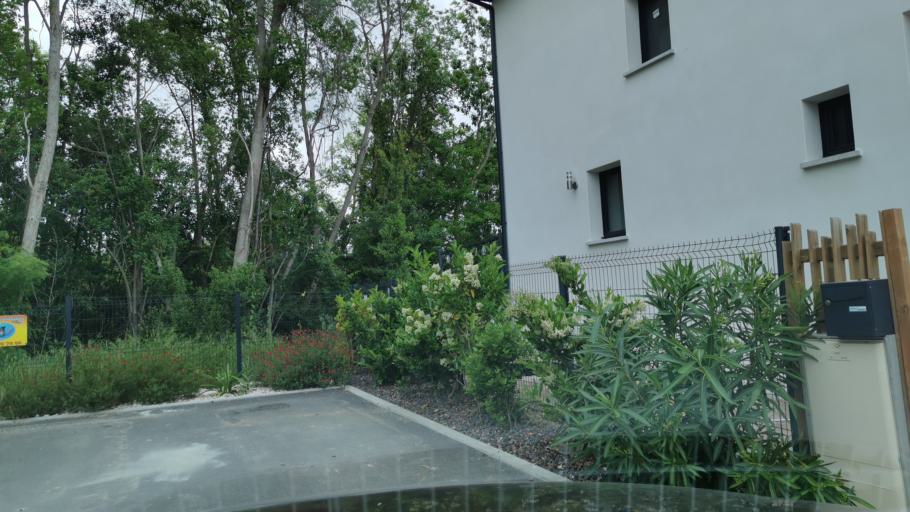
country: FR
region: Languedoc-Roussillon
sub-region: Departement de l'Aude
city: Narbonne
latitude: 43.1971
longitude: 3.0099
